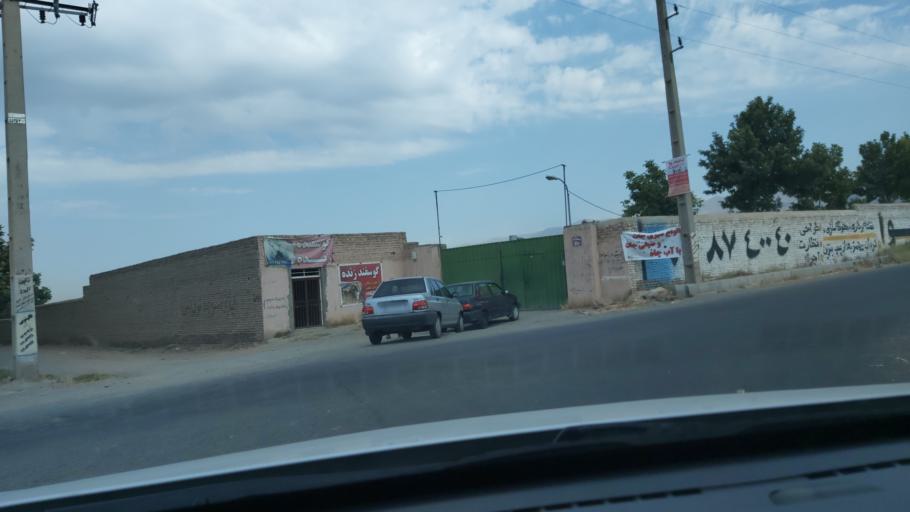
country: IR
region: Alborz
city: Hashtgerd
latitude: 35.9430
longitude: 50.7708
